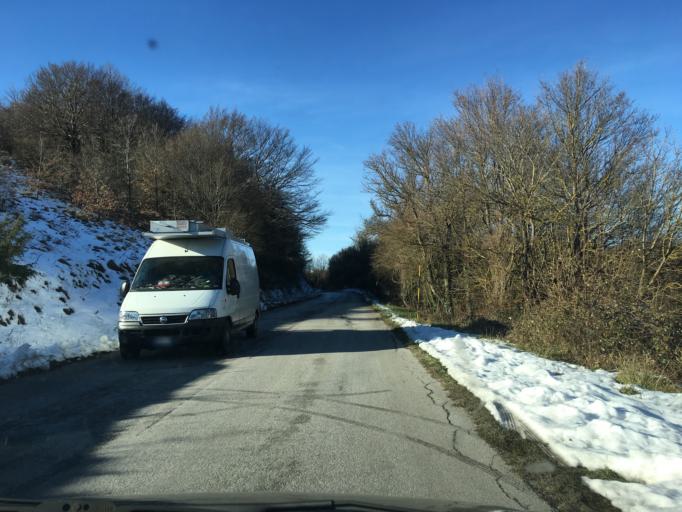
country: IT
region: Abruzzo
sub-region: Provincia di Chieti
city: Rosello
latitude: 41.8599
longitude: 14.3561
